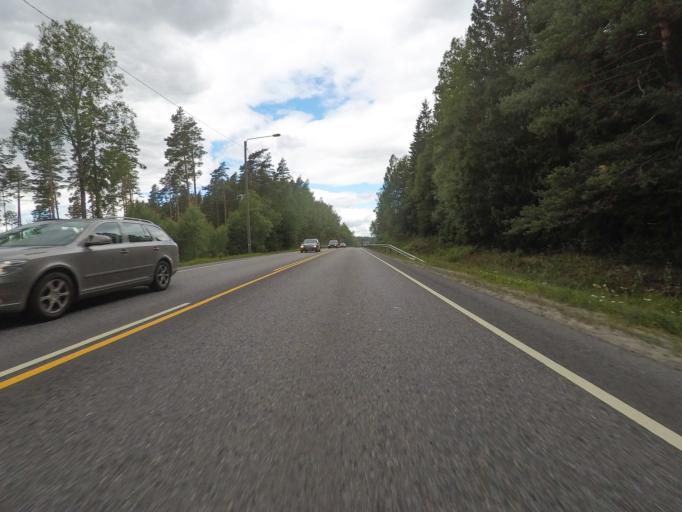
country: FI
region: Varsinais-Suomi
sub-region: Turku
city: Piikkioe
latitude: 60.4467
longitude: 22.4721
